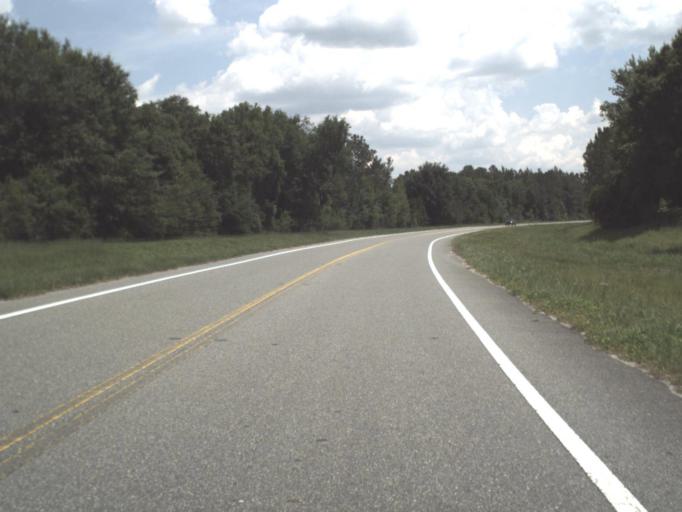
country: US
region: Florida
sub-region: Bradford County
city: Starke
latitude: 30.0191
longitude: -82.0499
